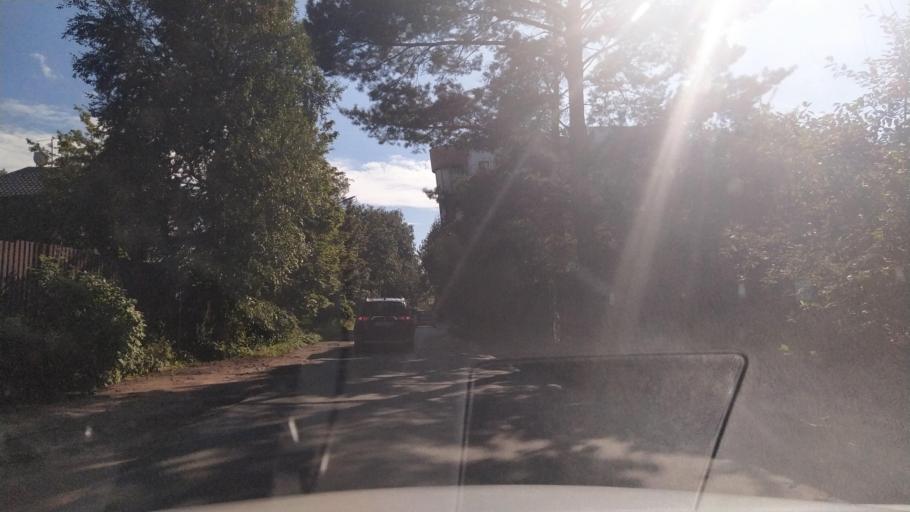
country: RU
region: St.-Petersburg
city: Kolomyagi
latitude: 60.0211
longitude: 30.2976
